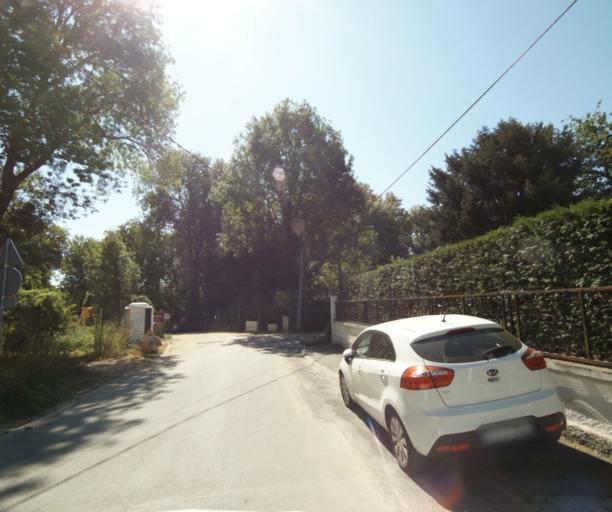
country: FR
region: Ile-de-France
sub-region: Departement de l'Essonne
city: Baulne
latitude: 48.5082
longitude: 2.3626
